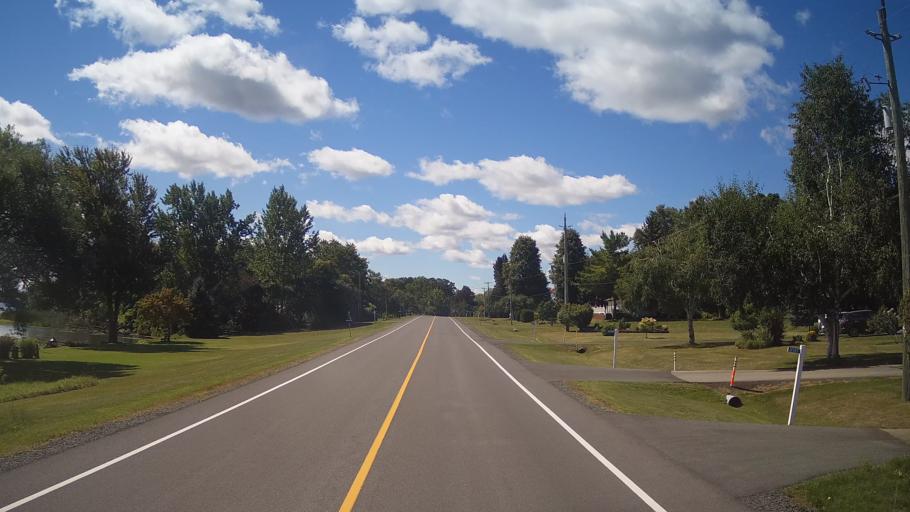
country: US
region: New York
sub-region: St. Lawrence County
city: Norfolk
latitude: 44.8697
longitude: -75.2466
